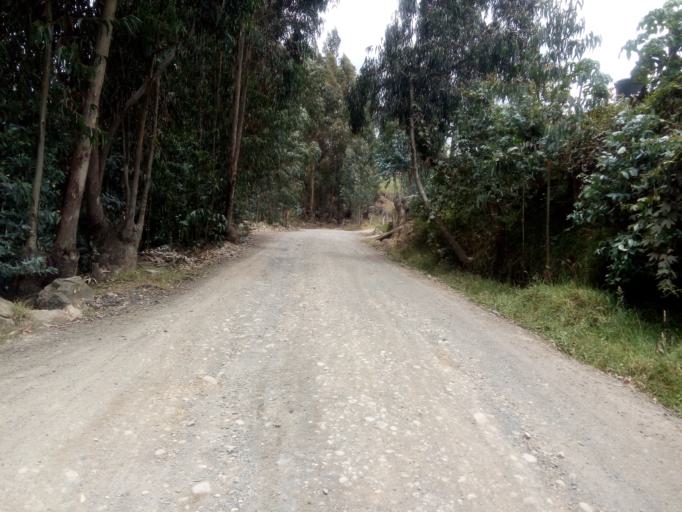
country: CO
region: Boyaca
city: Gameza
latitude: 5.8094
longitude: -72.8036
